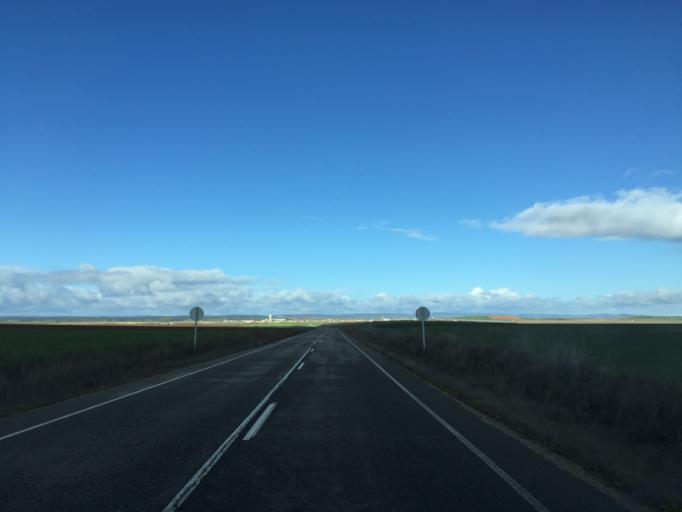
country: ES
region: Castille and Leon
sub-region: Provincia de Zamora
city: Manganeses de la Lampreana
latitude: 41.7602
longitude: -5.7368
